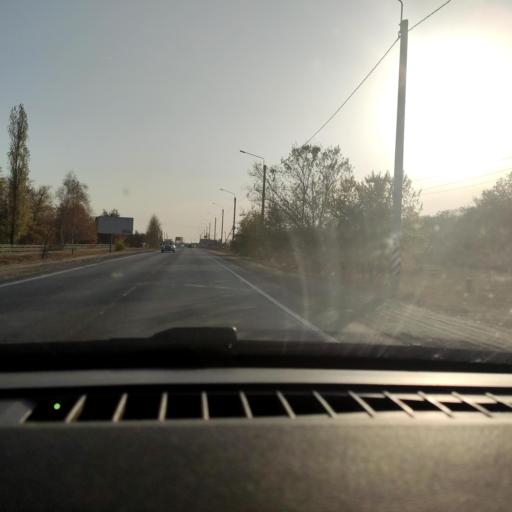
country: RU
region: Voronezj
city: Semiluki
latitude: 51.7292
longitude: 39.0379
